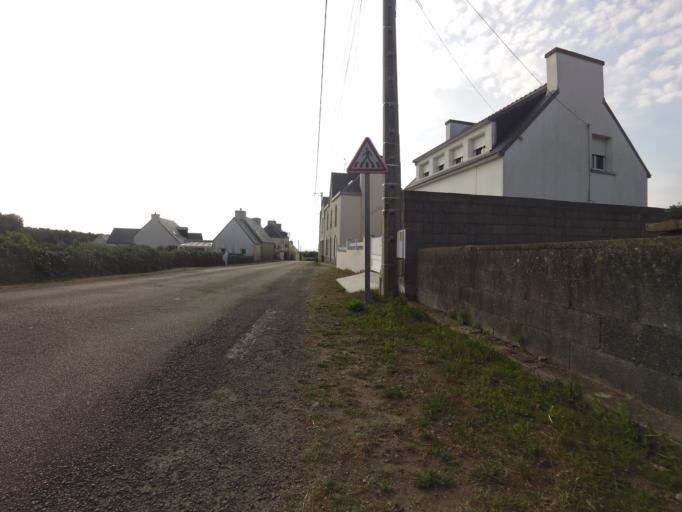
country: FR
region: Brittany
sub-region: Departement du Finistere
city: Plozevet
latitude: 47.9795
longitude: -4.4324
